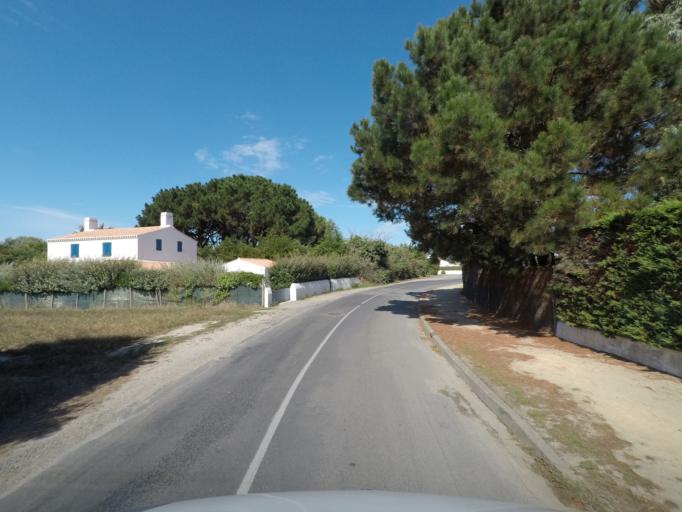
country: FR
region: Pays de la Loire
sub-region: Departement de la Vendee
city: La Gueriniere
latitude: 46.9997
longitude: -2.2265
